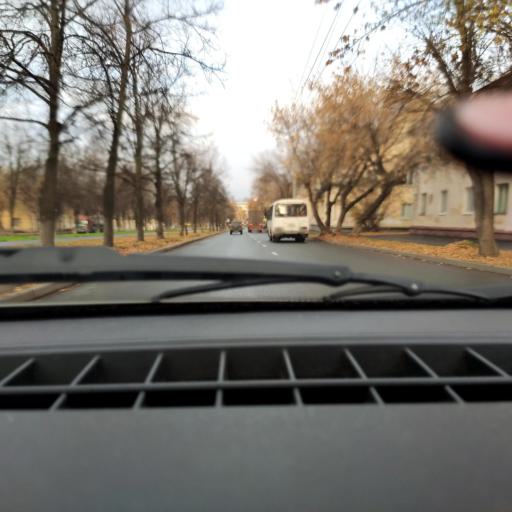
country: RU
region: Bashkortostan
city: Ufa
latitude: 54.8135
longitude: 56.1089
